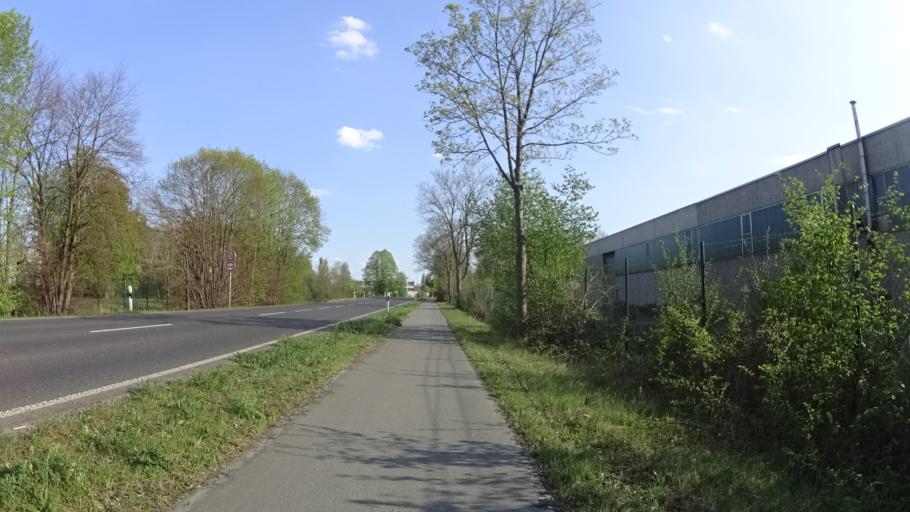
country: DE
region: North Rhine-Westphalia
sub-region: Regierungsbezirk Dusseldorf
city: Dormagen
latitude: 51.1385
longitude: 6.7998
